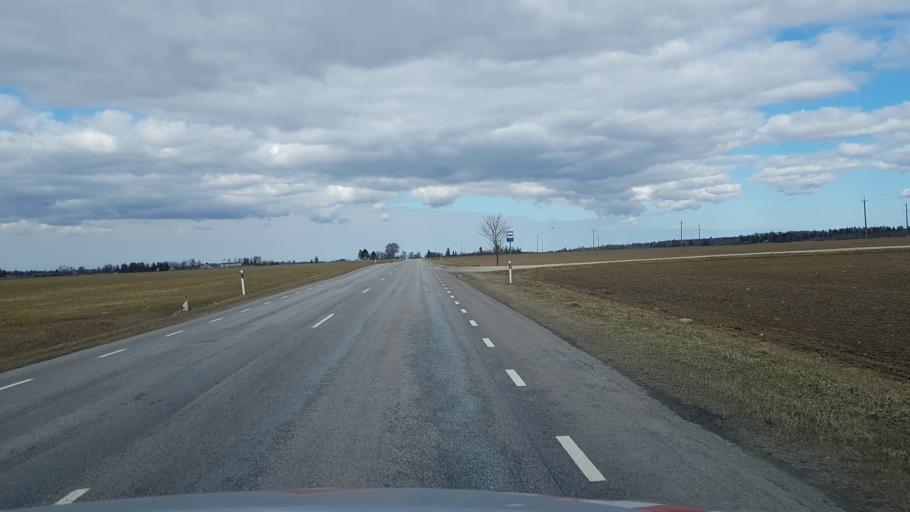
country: EE
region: Laeaene-Virumaa
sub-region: Vaeike-Maarja vald
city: Vaike-Maarja
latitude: 59.1673
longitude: 26.2675
